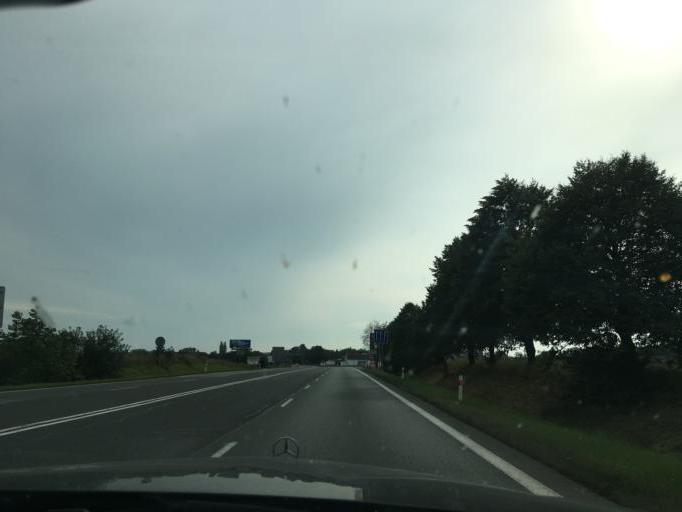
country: CZ
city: Predmerice nad Labem
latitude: 50.2307
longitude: 15.7910
